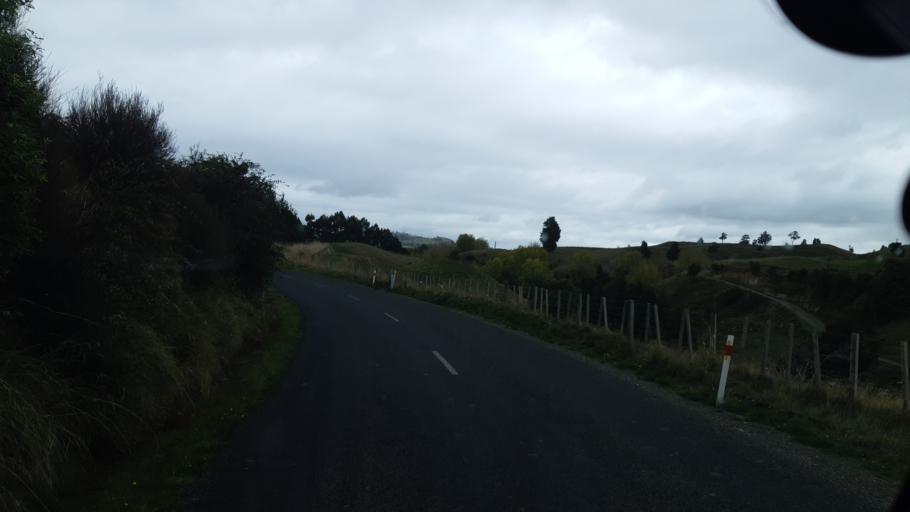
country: NZ
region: Manawatu-Wanganui
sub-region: Ruapehu District
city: Waiouru
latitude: -39.5526
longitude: 175.6117
